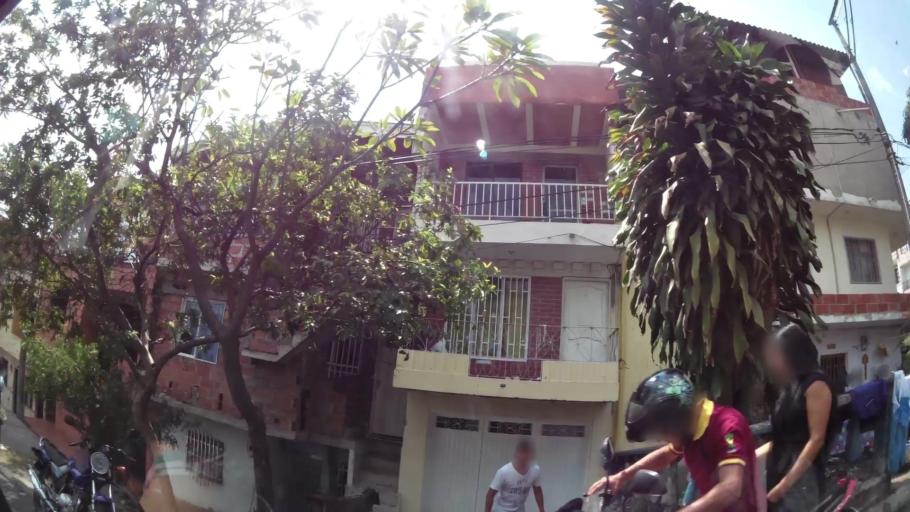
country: CO
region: Antioquia
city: Medellin
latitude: 6.2894
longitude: -75.5757
